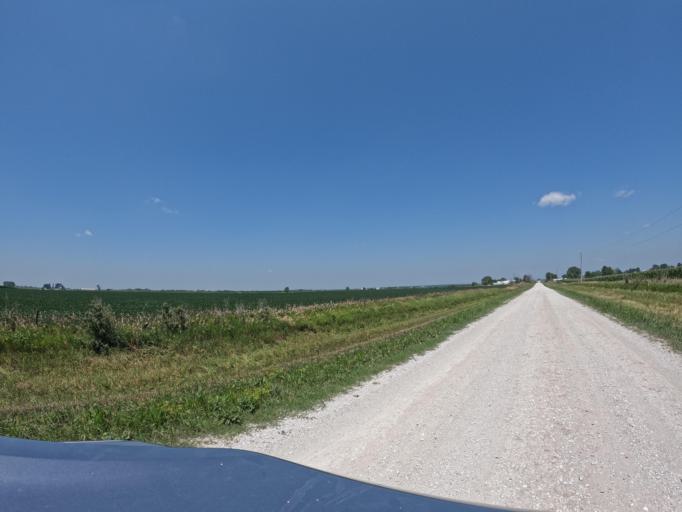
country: US
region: Iowa
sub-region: Keokuk County
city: Sigourney
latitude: 41.2654
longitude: -92.1699
